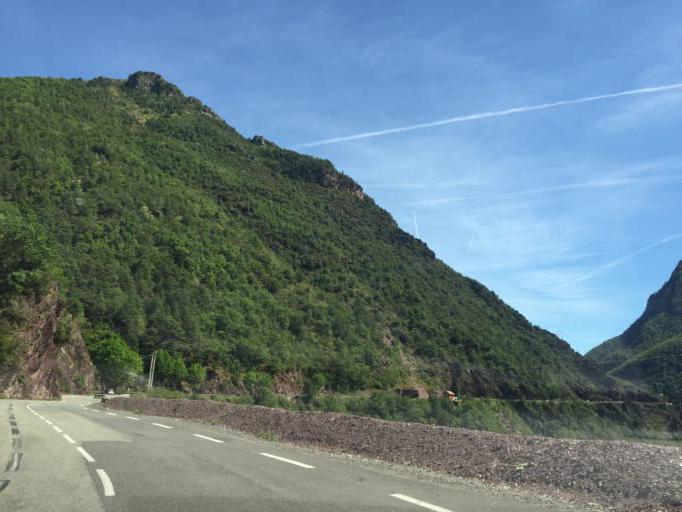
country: FR
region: Provence-Alpes-Cote d'Azur
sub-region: Departement des Alpes-Maritimes
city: Saint-Martin-Vesubie
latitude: 44.0652
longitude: 7.1145
